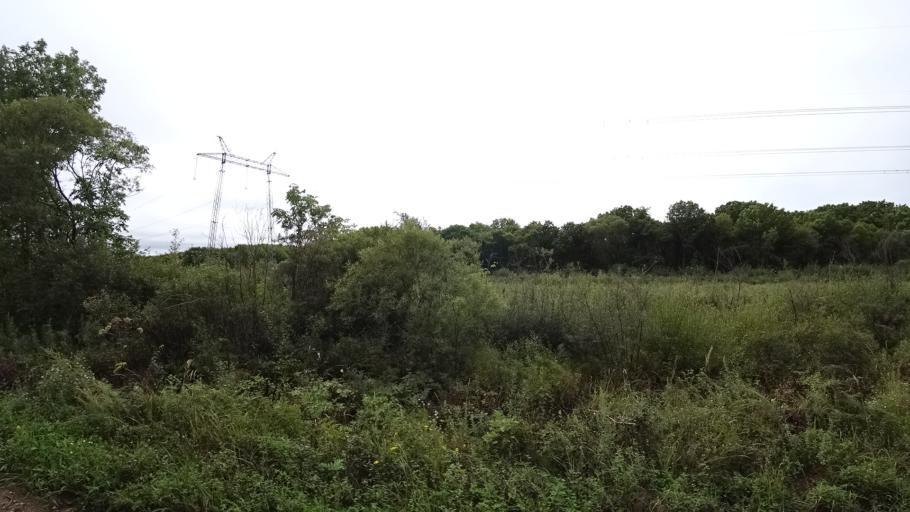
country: RU
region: Primorskiy
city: Lyalichi
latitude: 44.0784
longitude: 132.4537
